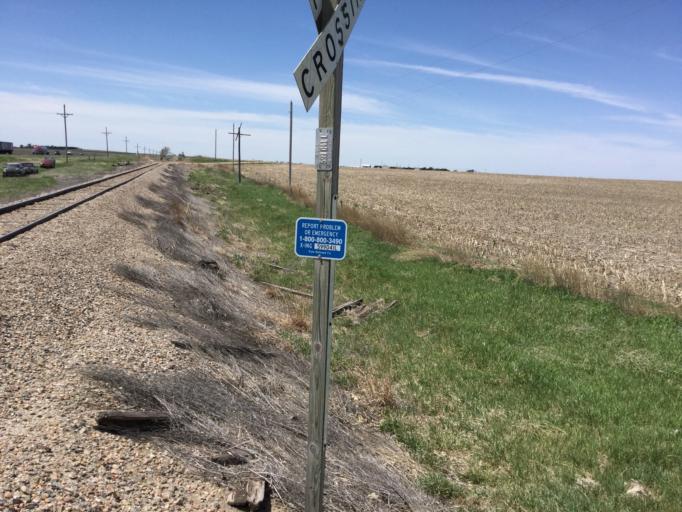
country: US
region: Kansas
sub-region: Sheridan County
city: Hoxie
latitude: 39.5832
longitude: -100.4796
